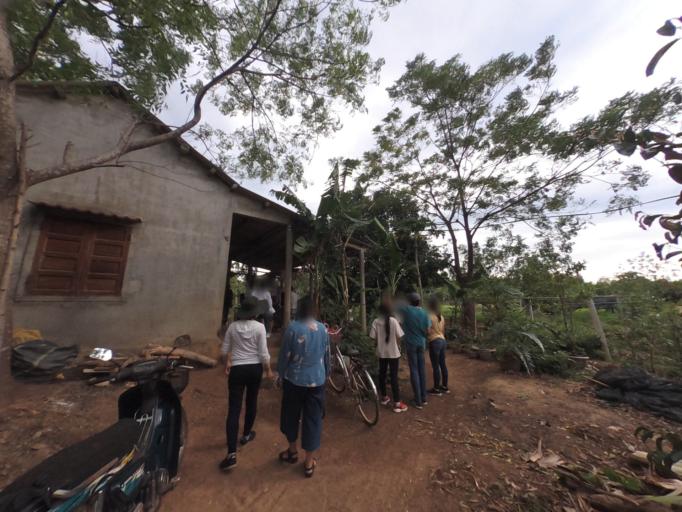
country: VN
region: Quang Tri
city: Cam Lo
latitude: 16.7888
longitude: 107.0023
